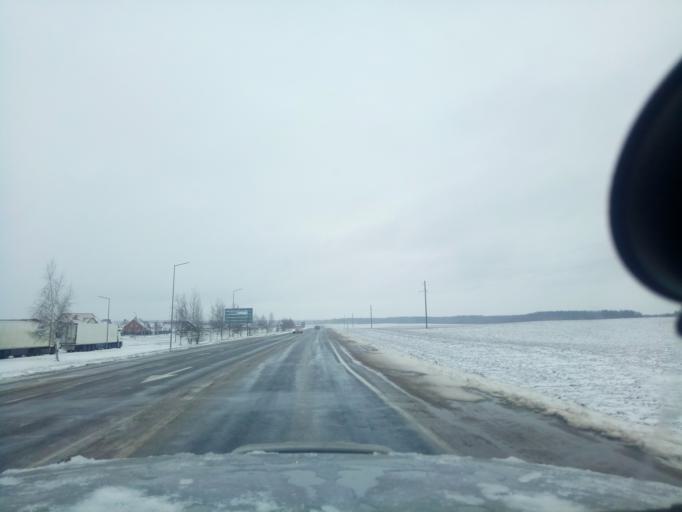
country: BY
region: Minsk
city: Nyasvizh
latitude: 53.2261
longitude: 26.6442
